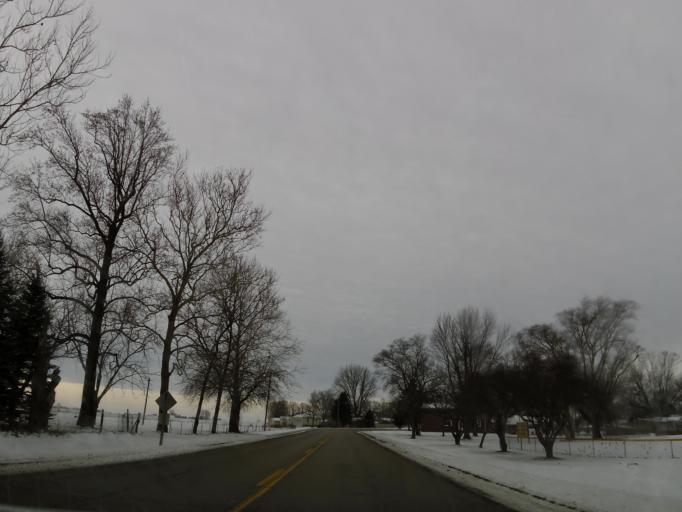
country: US
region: Illinois
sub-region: LaSalle County
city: Peru
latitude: 41.2638
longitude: -89.1215
